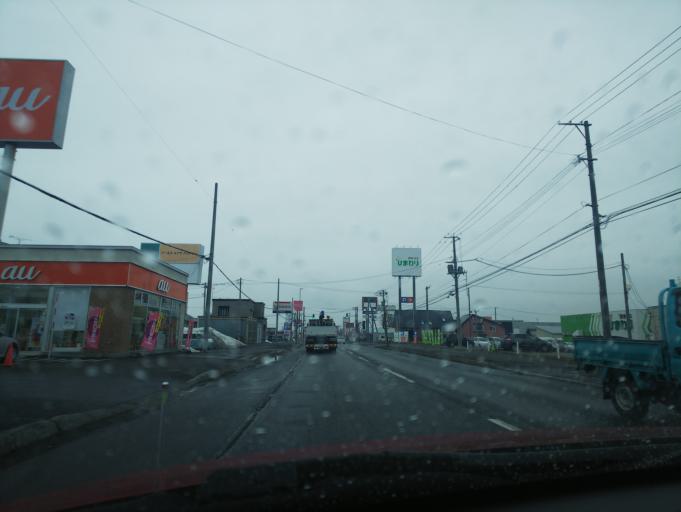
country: JP
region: Hokkaido
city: Nayoro
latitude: 44.1628
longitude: 142.3963
